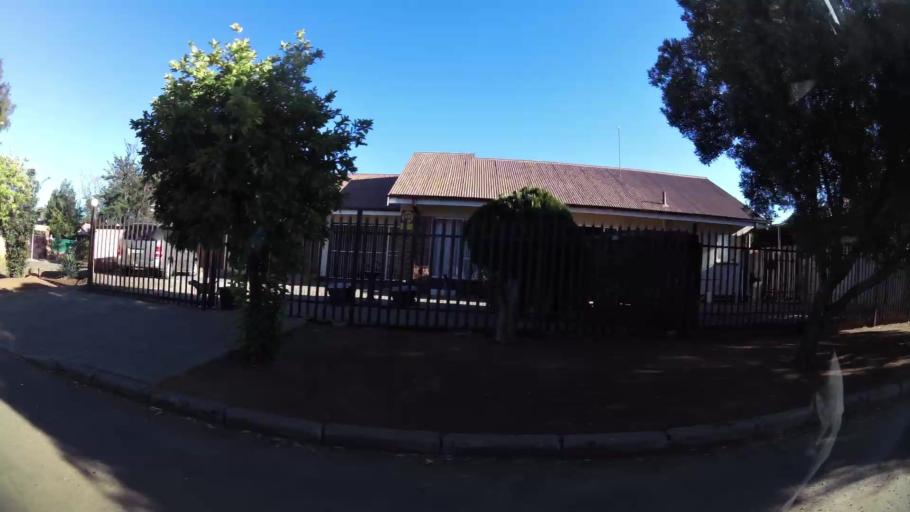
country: ZA
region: Northern Cape
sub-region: Frances Baard District Municipality
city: Kimberley
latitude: -28.7545
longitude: 24.7889
